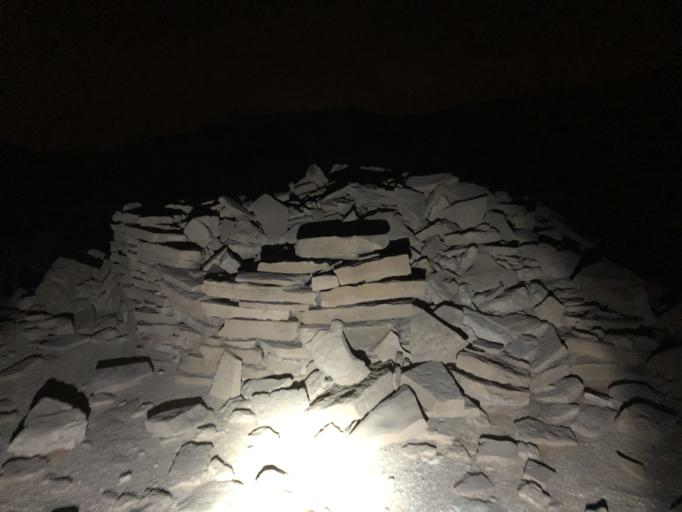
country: SA
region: Ar Riyad
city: Riyadh
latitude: 24.2584
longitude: 46.7686
